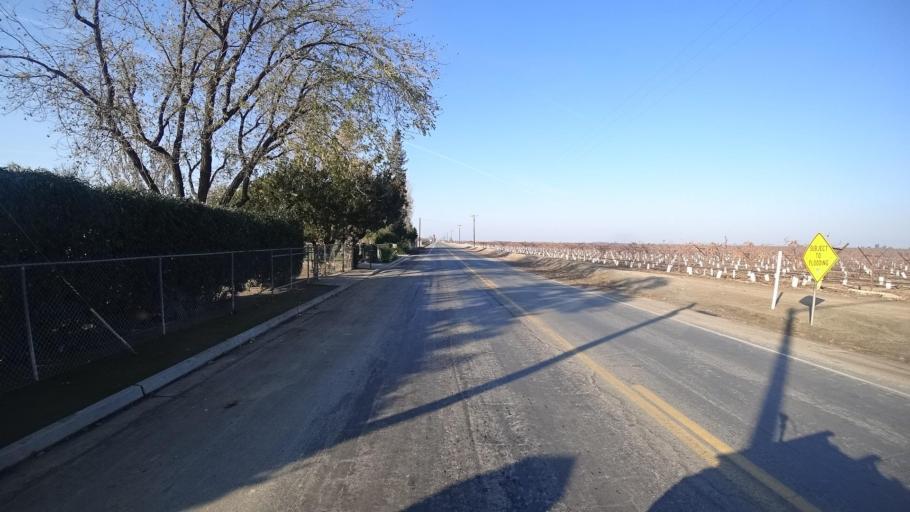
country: US
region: California
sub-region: Kern County
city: Lamont
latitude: 35.2524
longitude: -118.9323
